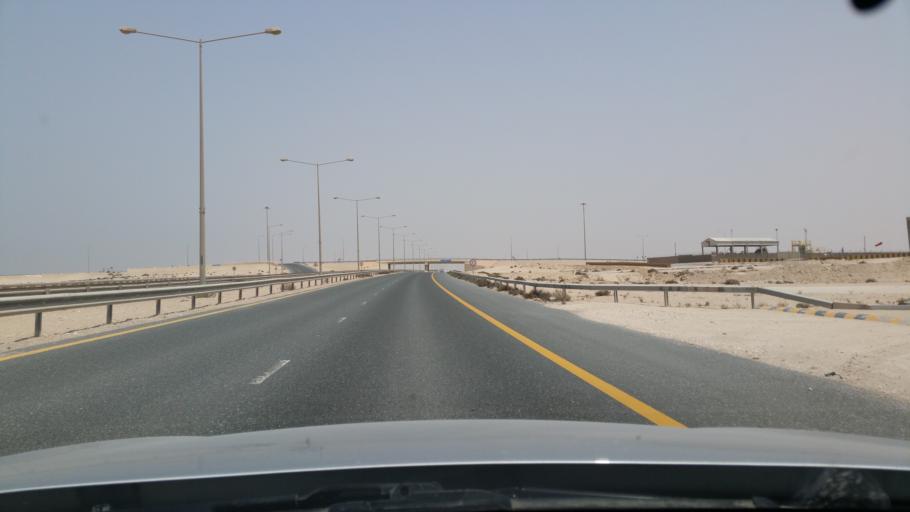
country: QA
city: Umm Bab
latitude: 25.2903
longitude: 50.7909
